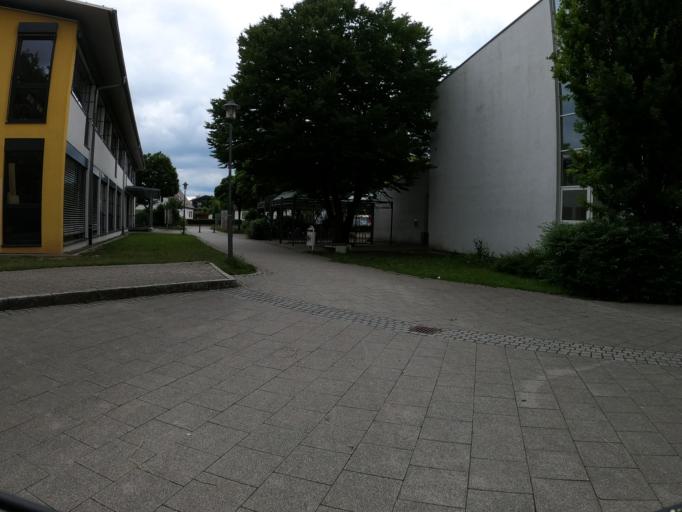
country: DE
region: Baden-Wuerttemberg
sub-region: Tuebingen Region
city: Langenau
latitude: 48.5013
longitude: 10.1212
